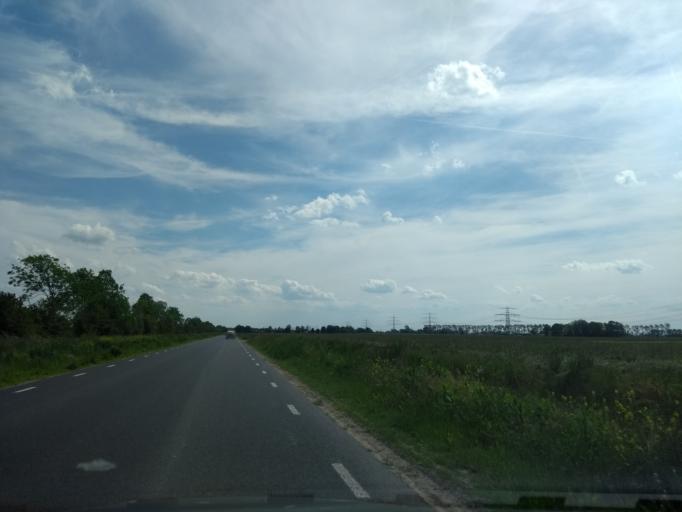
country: NL
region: Groningen
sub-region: Gemeente Zuidhorn
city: Aduard
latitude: 53.2570
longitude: 6.4813
